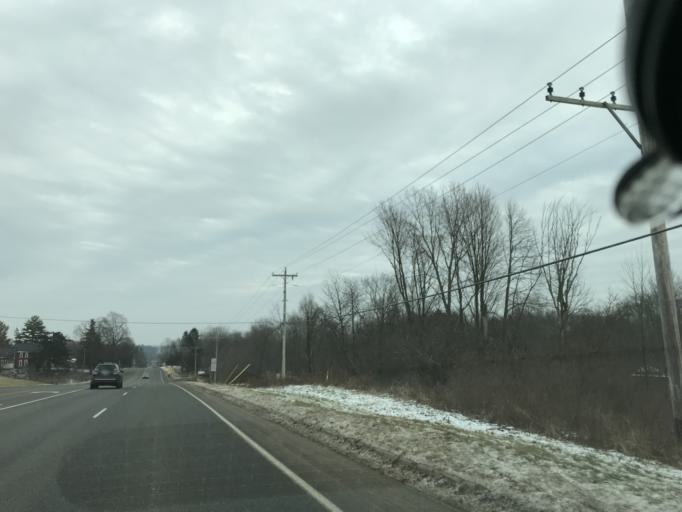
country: US
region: Michigan
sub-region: Kent County
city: Rockford
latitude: 43.1172
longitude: -85.5762
